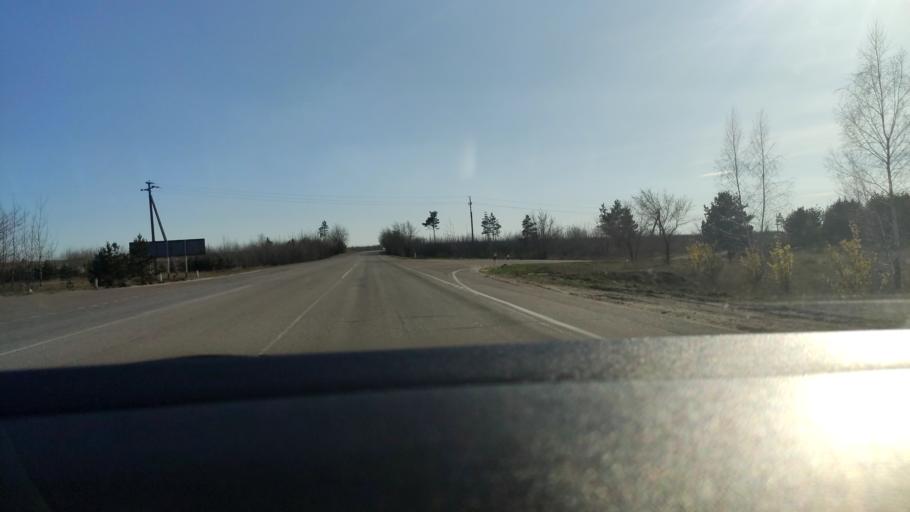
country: RU
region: Voronezj
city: Kolodeznyy
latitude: 51.3772
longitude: 39.2137
